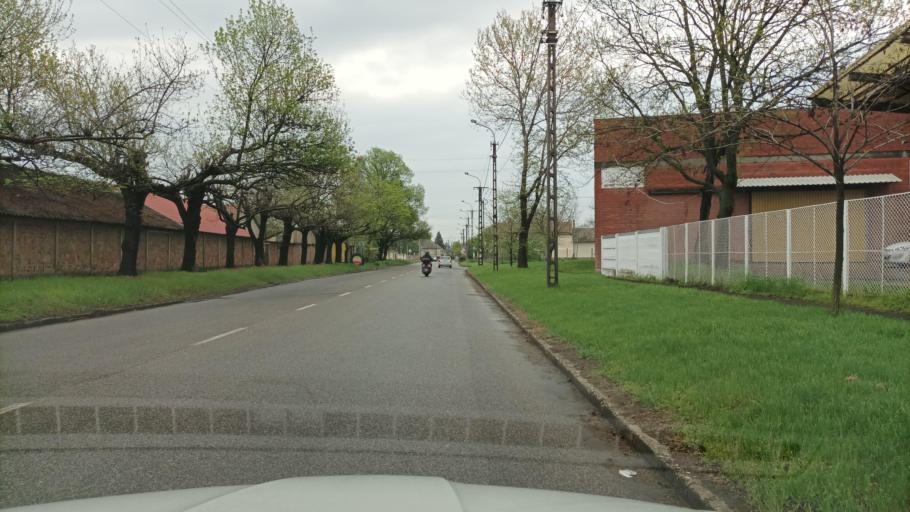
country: HU
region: Pest
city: Nagykoros
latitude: 47.0351
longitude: 19.7607
